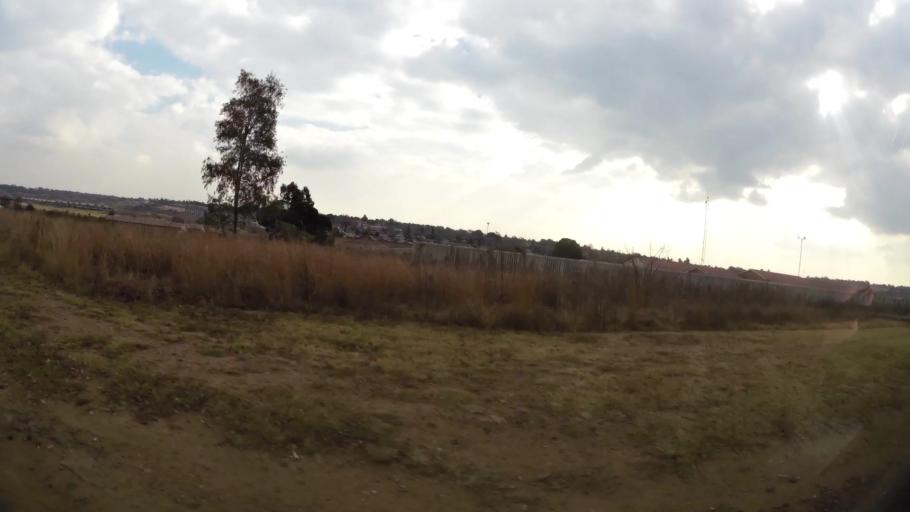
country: ZA
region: Gauteng
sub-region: Ekurhuleni Metropolitan Municipality
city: Benoni
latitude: -26.1406
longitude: 28.3569
